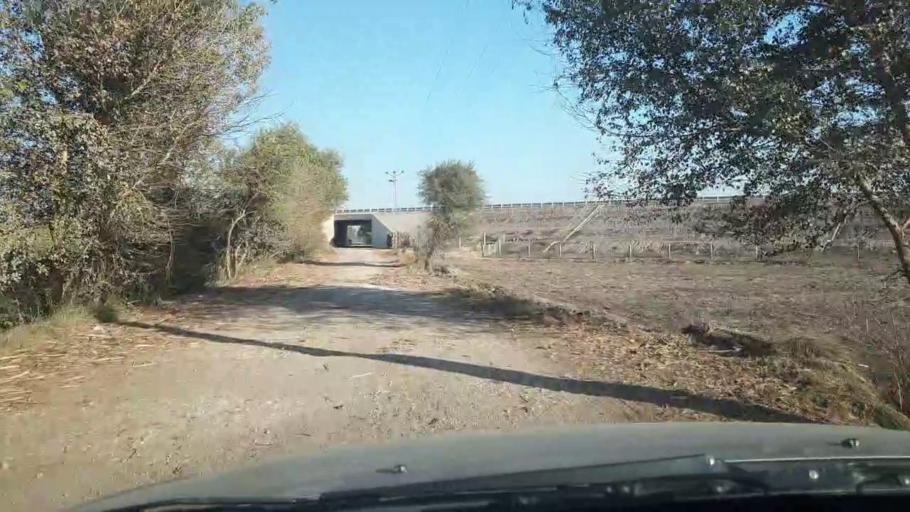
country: PK
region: Sindh
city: Ghotki
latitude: 28.0387
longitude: 69.3160
